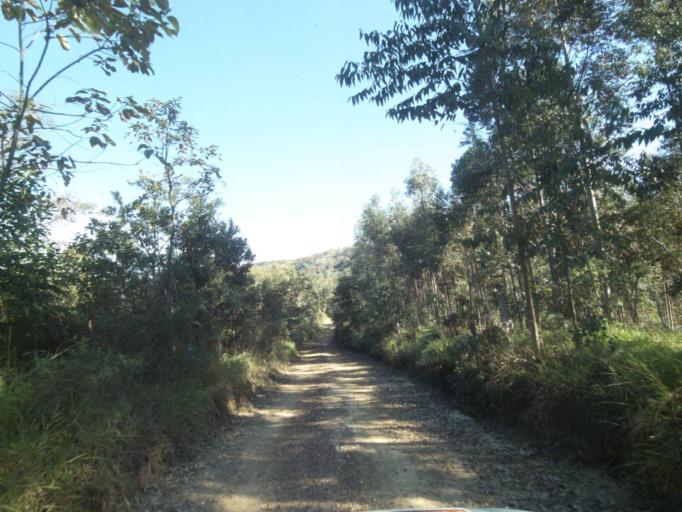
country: BR
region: Parana
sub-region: Tibagi
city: Tibagi
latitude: -24.5745
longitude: -50.4759
